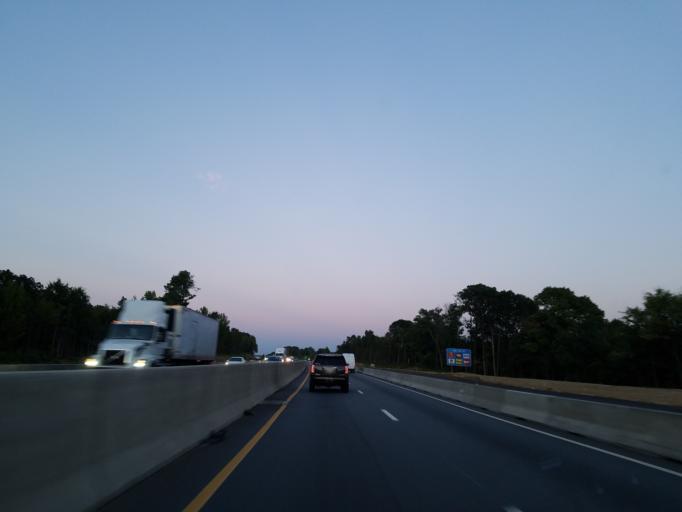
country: US
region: North Carolina
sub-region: Cabarrus County
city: Kannapolis
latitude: 35.4392
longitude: -80.6357
